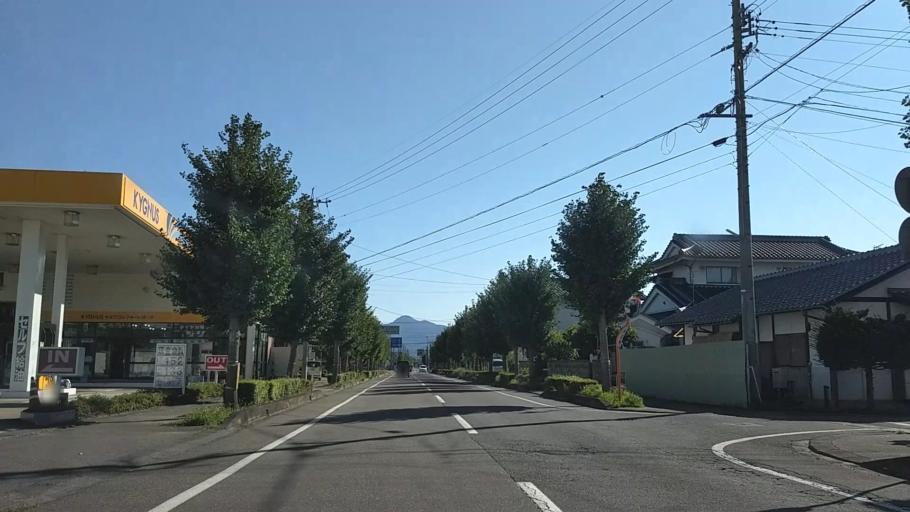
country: JP
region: Nagano
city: Nagano-shi
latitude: 36.5850
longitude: 138.1372
